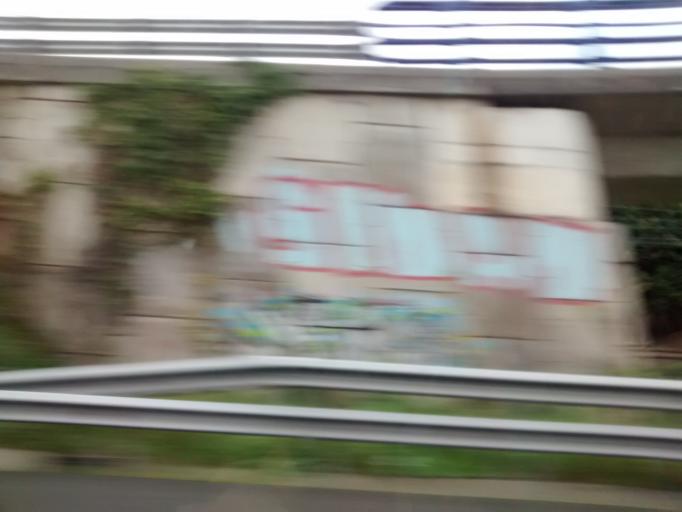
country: ES
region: Cantabria
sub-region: Provincia de Cantabria
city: El Astillero
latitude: 43.4052
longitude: -3.8230
